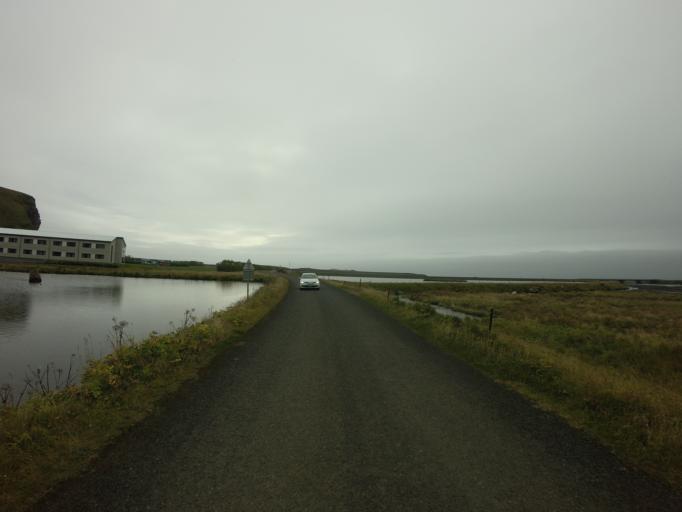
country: IS
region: South
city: Vestmannaeyjar
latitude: 63.4261
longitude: -18.9083
